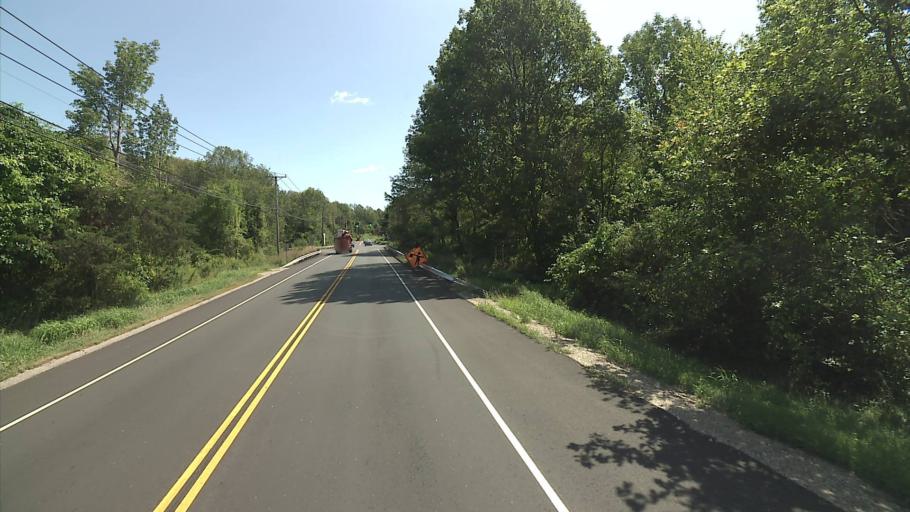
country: US
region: Connecticut
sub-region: New London County
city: Jewett City
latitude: 41.5819
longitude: -71.9011
